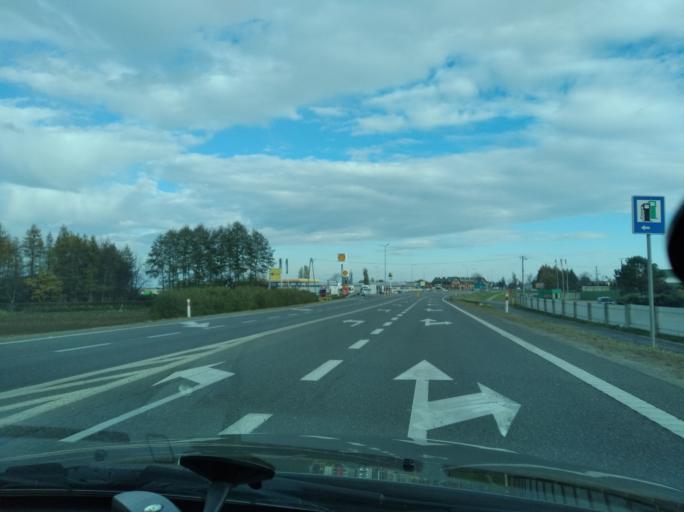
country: PL
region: Subcarpathian Voivodeship
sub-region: Powiat debicki
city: Debica
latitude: 50.0541
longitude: 21.4527
